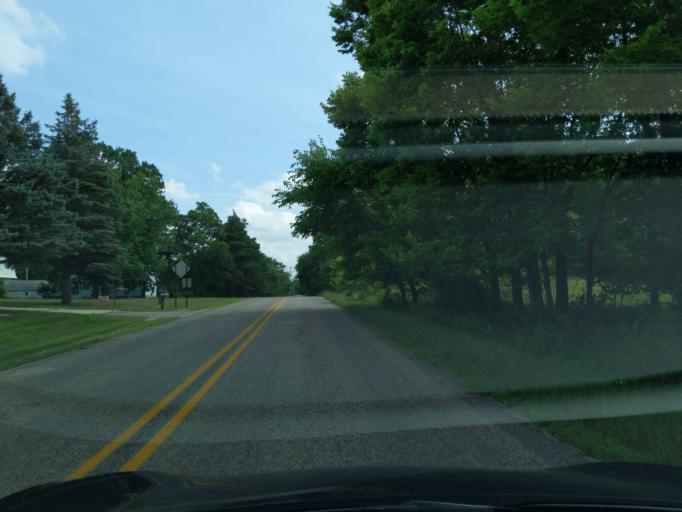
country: US
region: Michigan
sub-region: Eaton County
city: Dimondale
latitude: 42.5755
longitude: -84.6022
